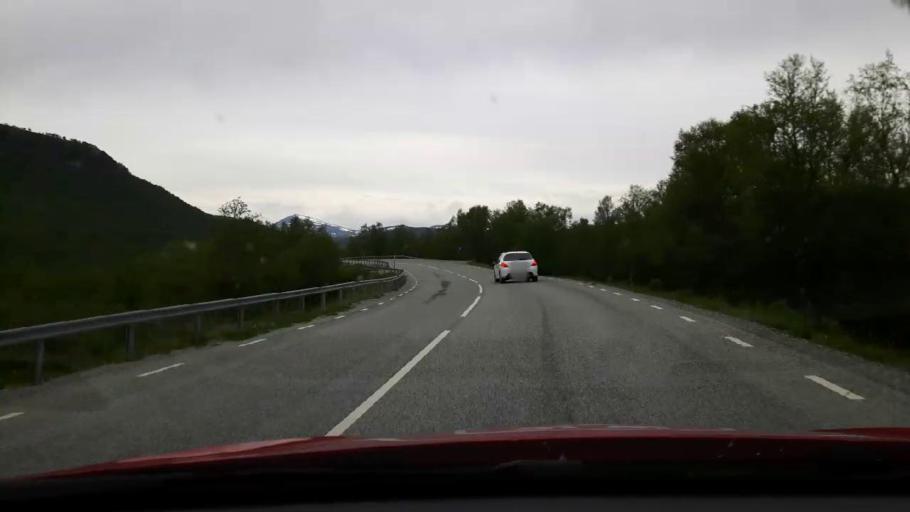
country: NO
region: Sor-Trondelag
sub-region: Tydal
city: Aas
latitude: 62.6815
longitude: 12.4169
